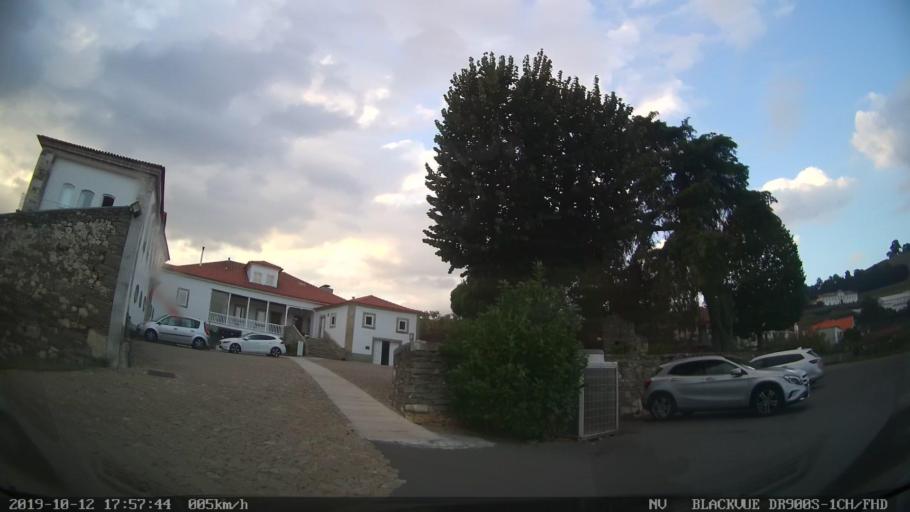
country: PT
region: Vila Real
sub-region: Mesao Frio
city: Mesao Frio
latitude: 41.1646
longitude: -7.8468
